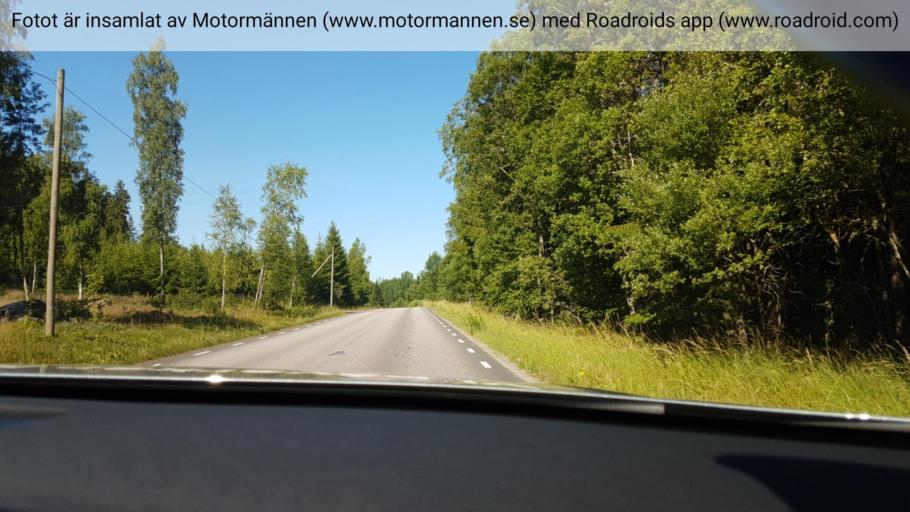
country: SE
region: Vaestra Goetaland
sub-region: Ulricehamns Kommun
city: Ulricehamn
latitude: 57.8300
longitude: 13.3035
